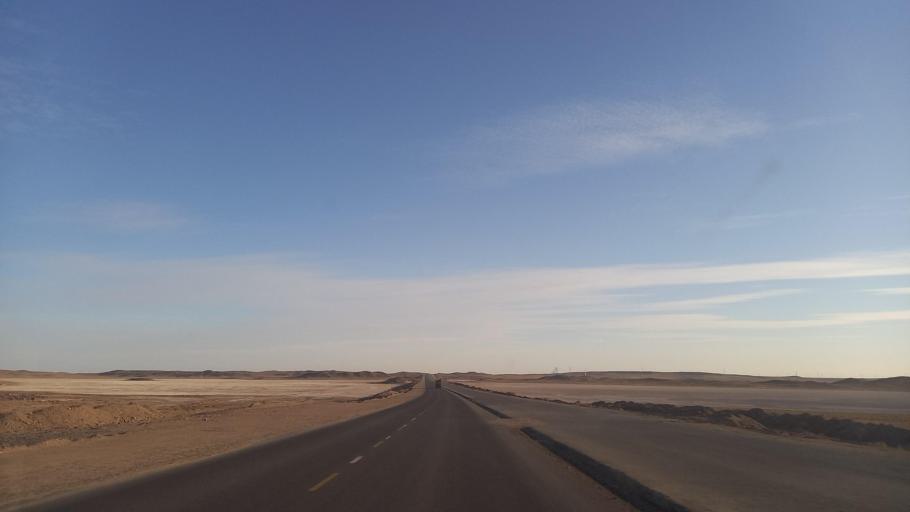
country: KZ
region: Zhambyl
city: Mynaral
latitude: 45.3190
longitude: 73.7416
